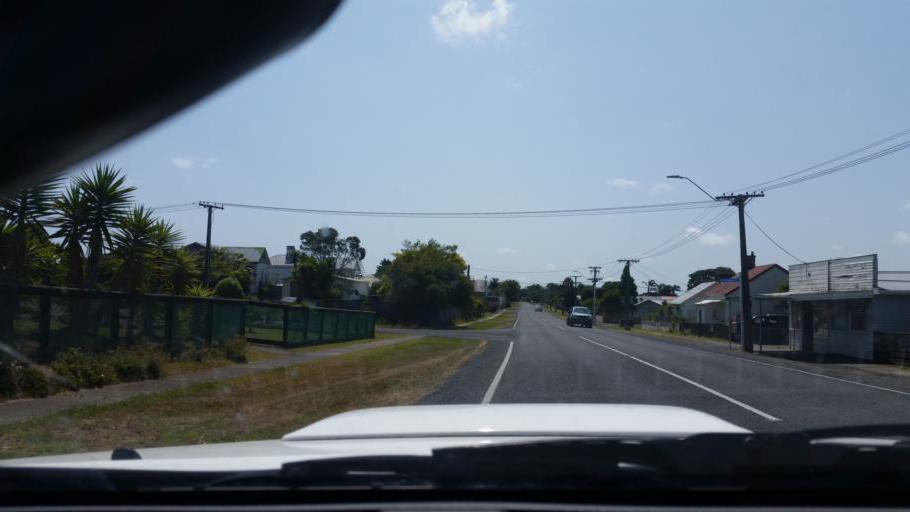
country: NZ
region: Northland
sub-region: Kaipara District
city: Dargaville
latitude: -36.0290
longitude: 173.9213
